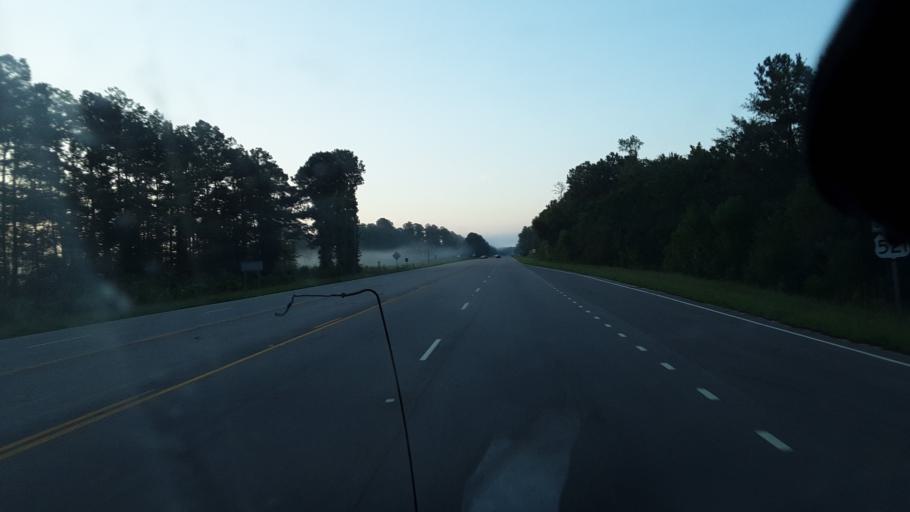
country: US
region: South Carolina
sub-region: Clarendon County
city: Manning
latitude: 33.7366
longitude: -80.2063
